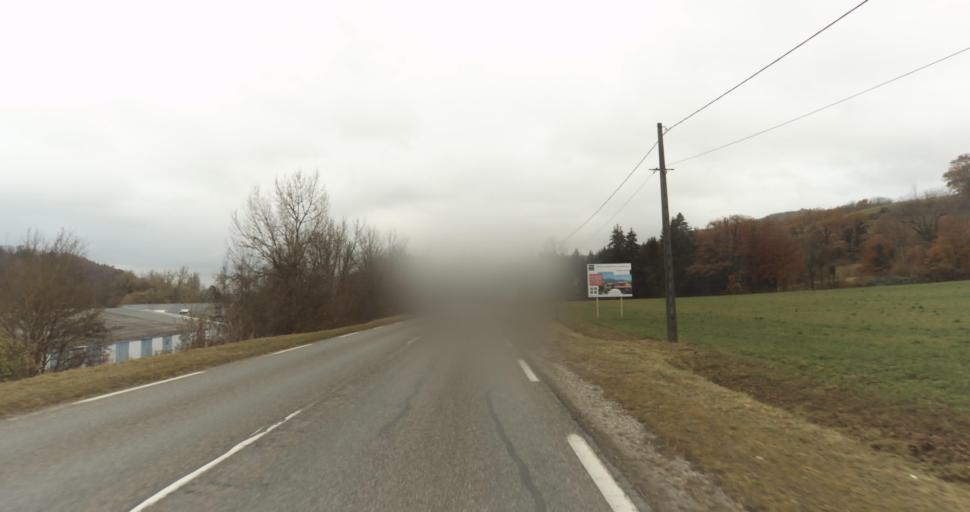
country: FR
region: Rhone-Alpes
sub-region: Departement de la Haute-Savoie
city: Saint-Martin-Bellevue
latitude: 45.9864
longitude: 6.1679
